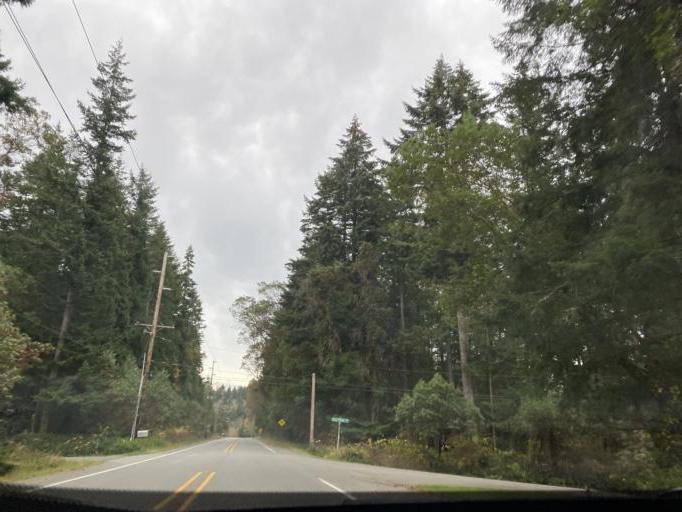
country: US
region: Washington
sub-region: Island County
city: Freeland
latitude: 48.0174
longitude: -122.5820
